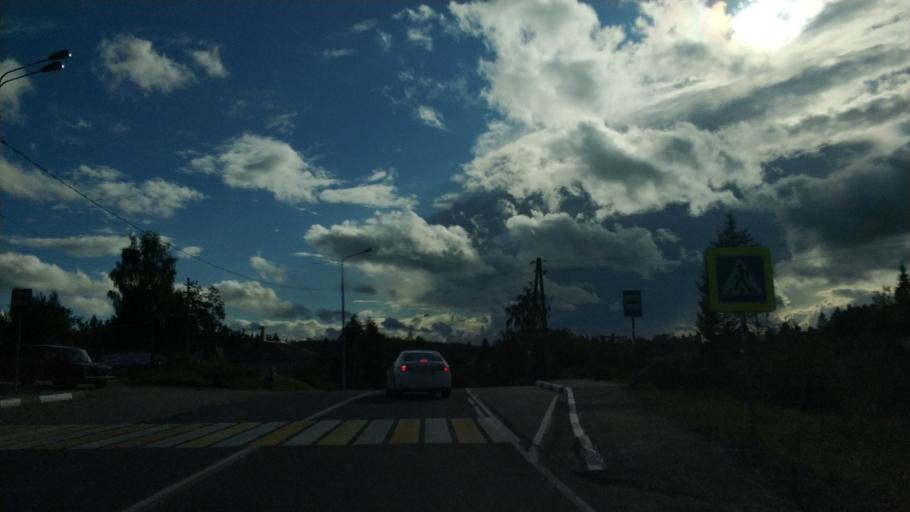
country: RU
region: Republic of Karelia
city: Lakhdenpokh'ya
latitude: 61.5197
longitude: 30.1565
